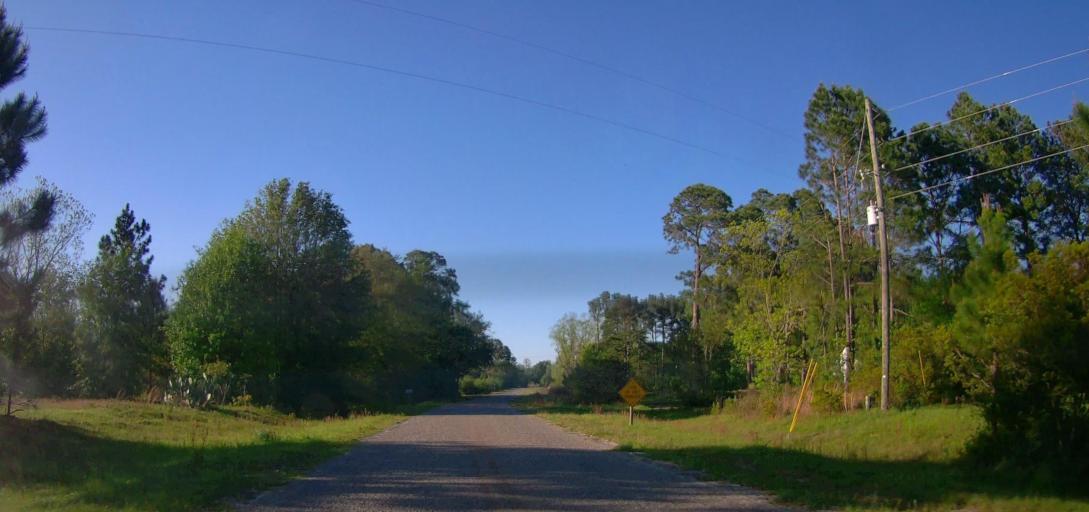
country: US
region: Georgia
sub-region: Ben Hill County
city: Fitzgerald
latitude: 31.6897
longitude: -83.1535
